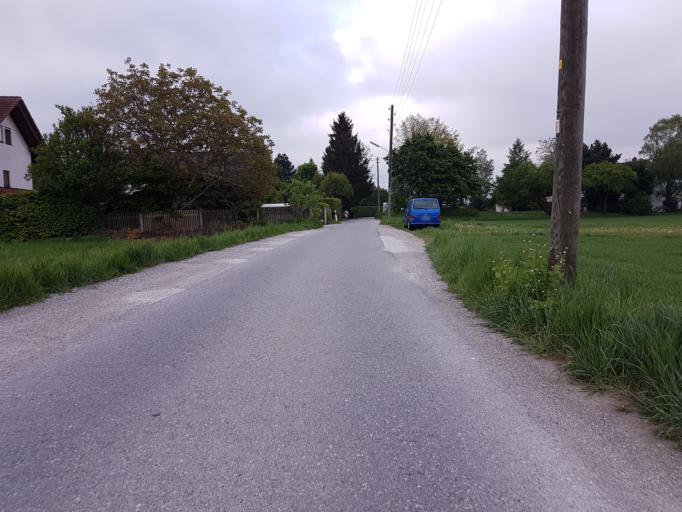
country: DE
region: Bavaria
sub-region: Upper Bavaria
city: Karlsfeld
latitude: 48.1858
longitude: 11.4554
